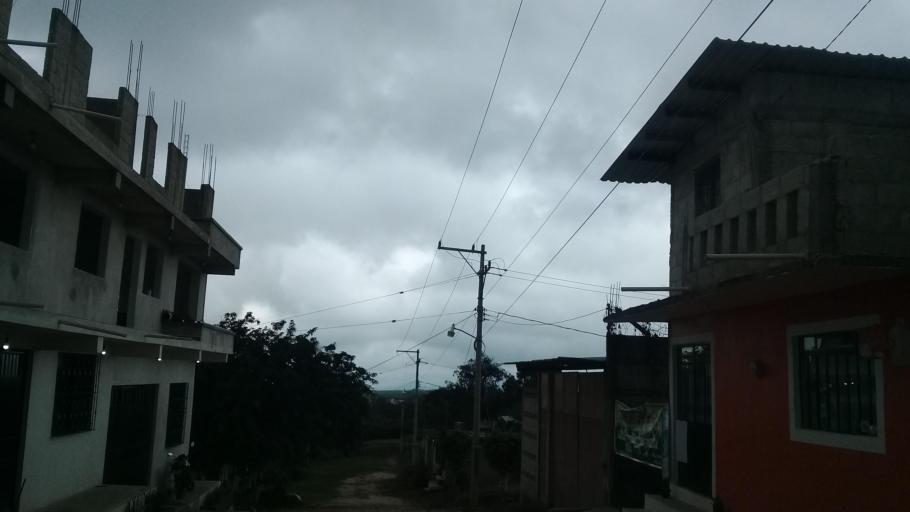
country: MX
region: Veracruz
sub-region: Emiliano Zapata
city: Jacarandas
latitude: 19.4913
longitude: -96.8539
